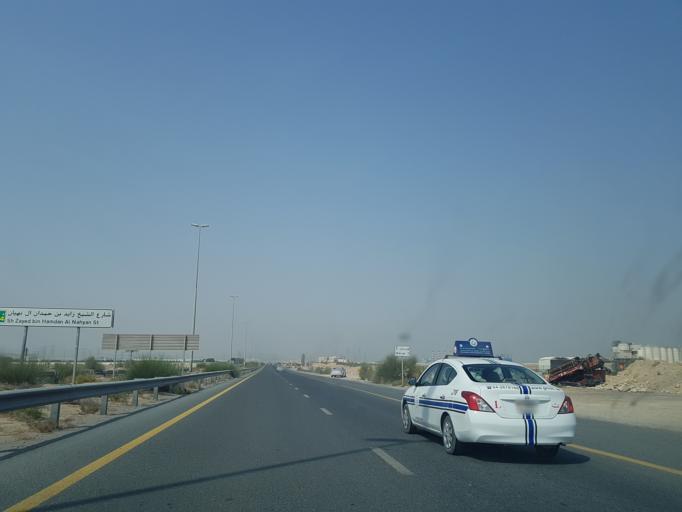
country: AE
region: Ash Shariqah
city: Sharjah
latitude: 25.1566
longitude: 55.4508
